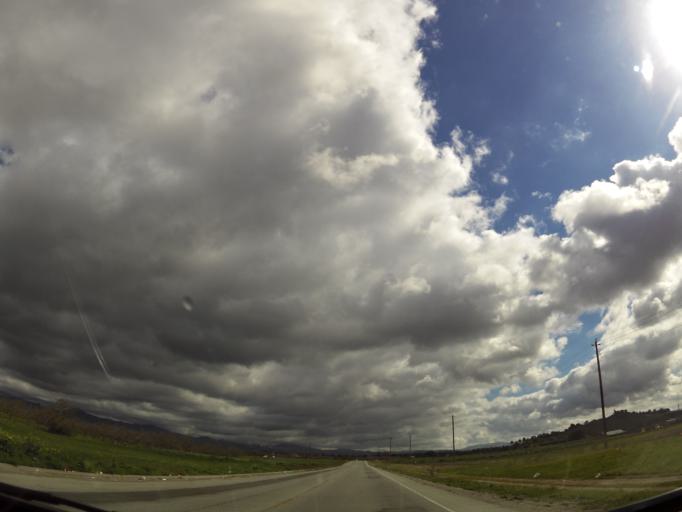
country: US
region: California
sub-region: San Benito County
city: Hollister
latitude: 36.8277
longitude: -121.3981
